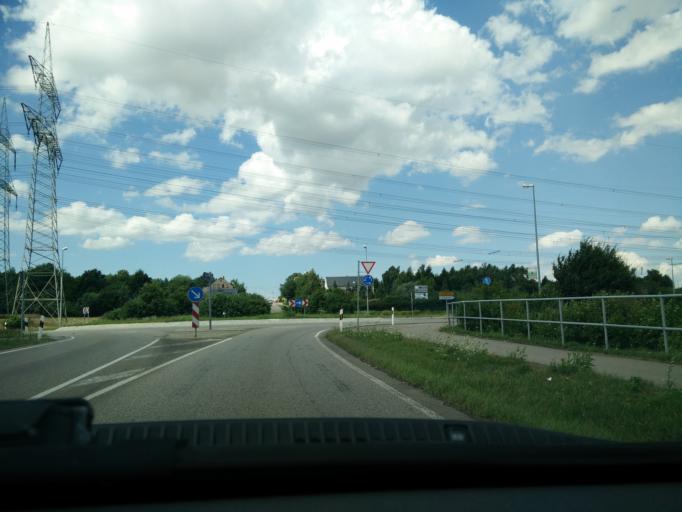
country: DE
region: Saxony
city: Hartmannsdorf
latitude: 50.8760
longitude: 12.8267
